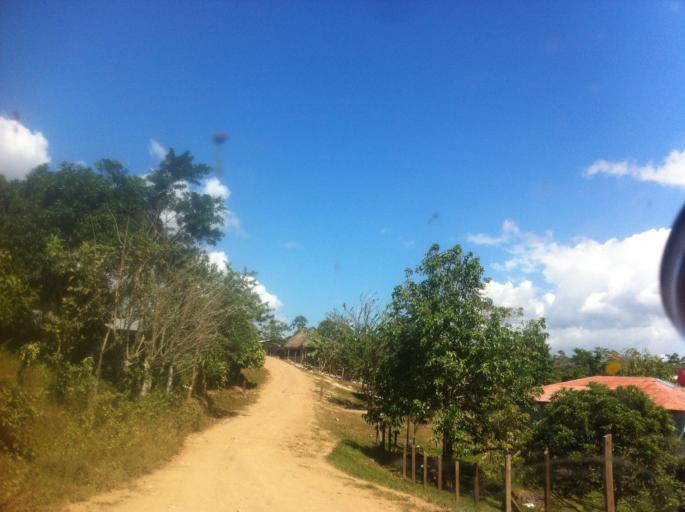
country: CR
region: Alajuela
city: Los Chiles
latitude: 11.2521
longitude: -84.4383
